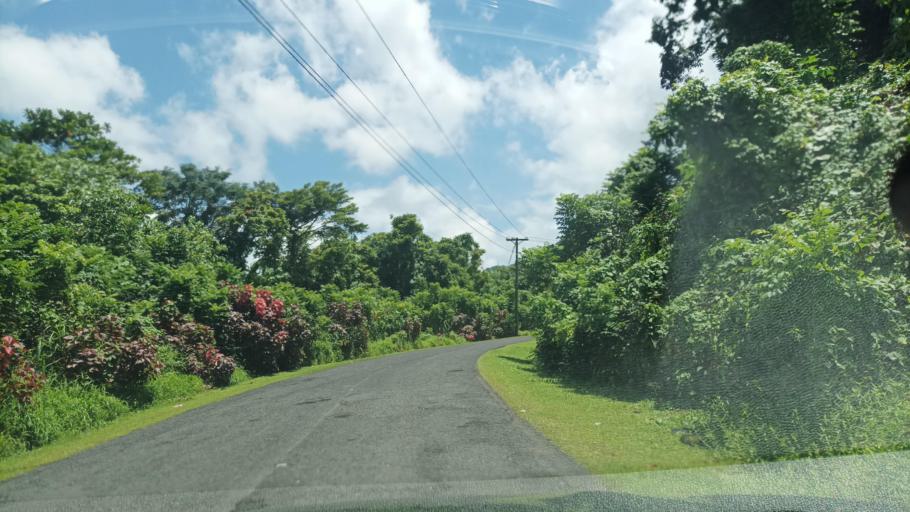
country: FM
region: Pohnpei
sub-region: Kolonia Municipality
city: Kolonia Town
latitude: 6.9461
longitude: 158.1852
